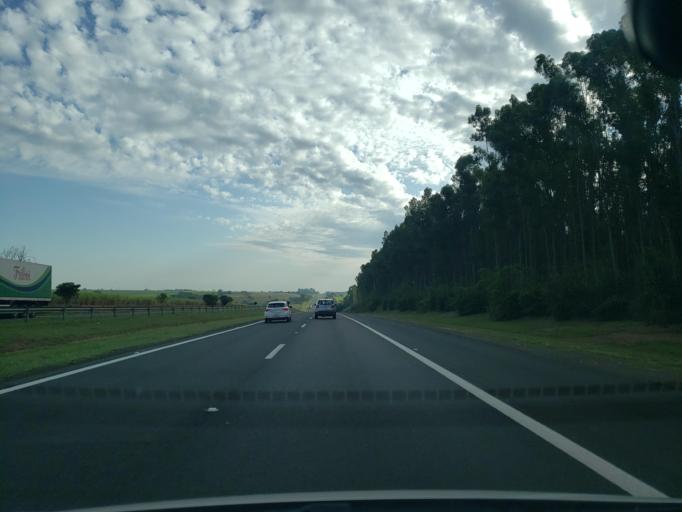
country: BR
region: Sao Paulo
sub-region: Guararapes
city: Guararapes
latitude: -21.1998
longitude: -50.5692
